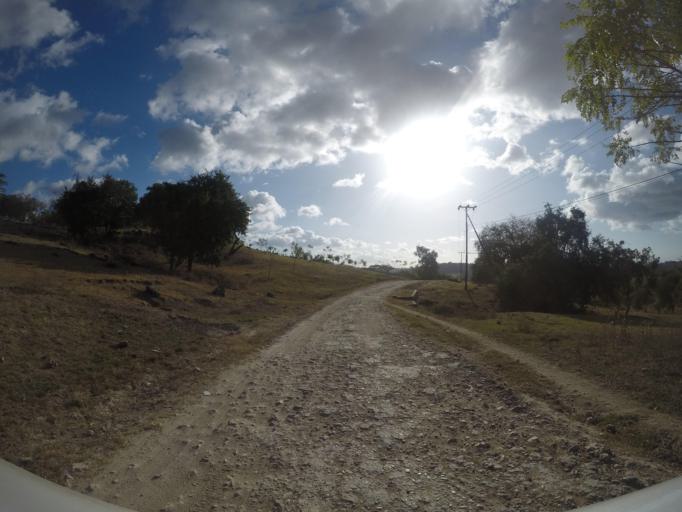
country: TL
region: Lautem
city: Lospalos
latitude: -8.4295
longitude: 126.8432
